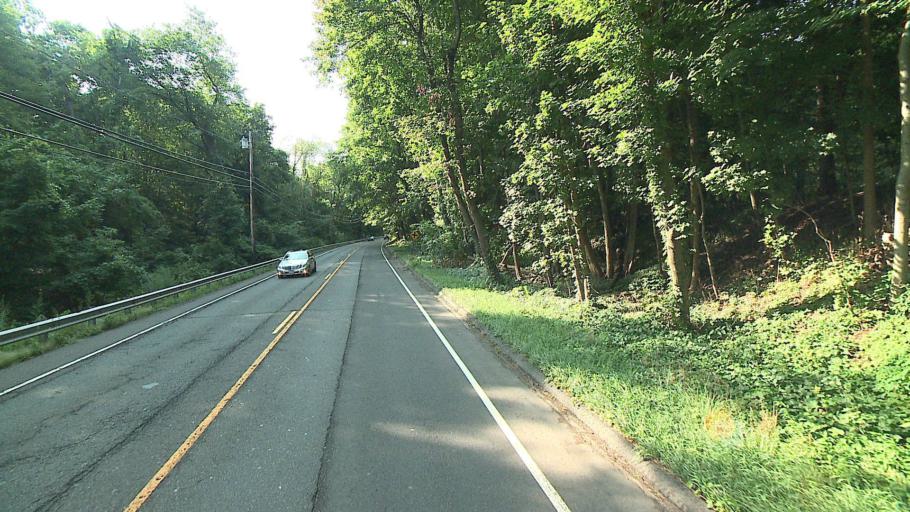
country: US
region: Connecticut
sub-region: Fairfield County
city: Georgetown
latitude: 41.2326
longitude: -73.4279
